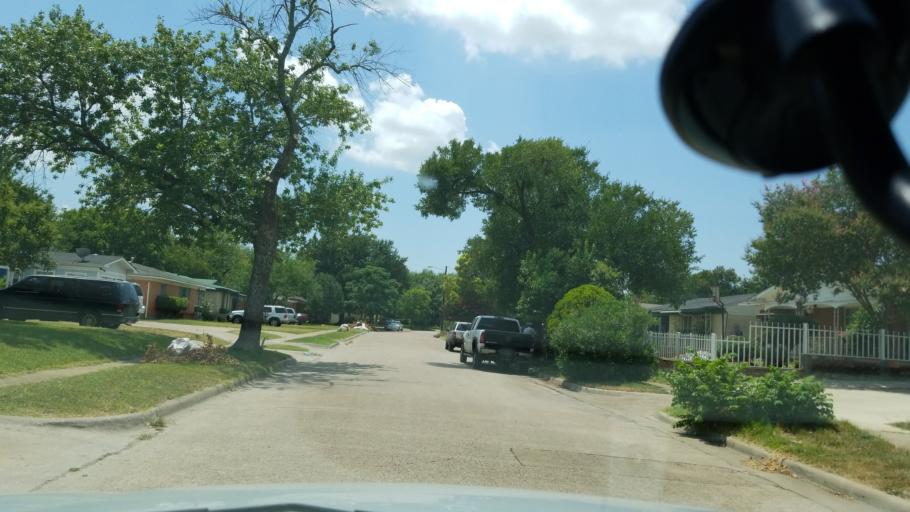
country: US
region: Texas
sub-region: Dallas County
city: Cockrell Hill
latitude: 32.7222
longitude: -96.8696
